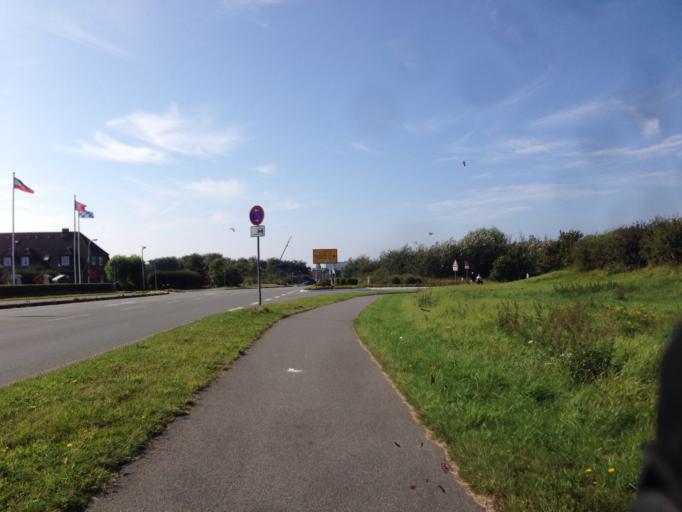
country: DE
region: Schleswig-Holstein
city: Tinnum
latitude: 54.9032
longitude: 8.3249
